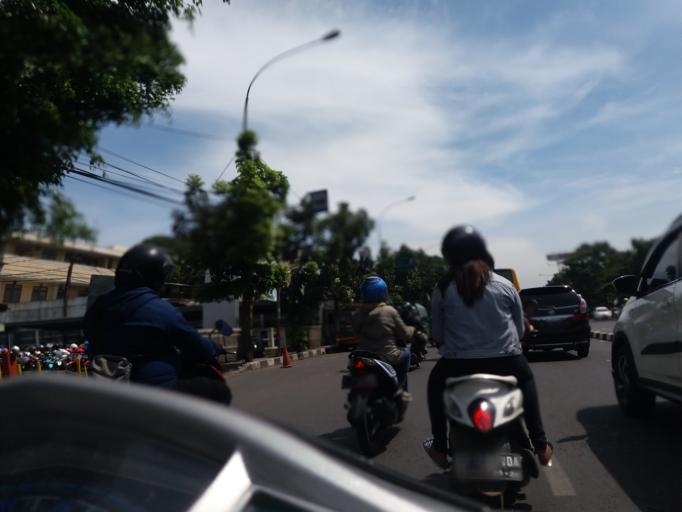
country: ID
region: West Java
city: Margahayukencana
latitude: -6.9471
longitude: 107.5941
